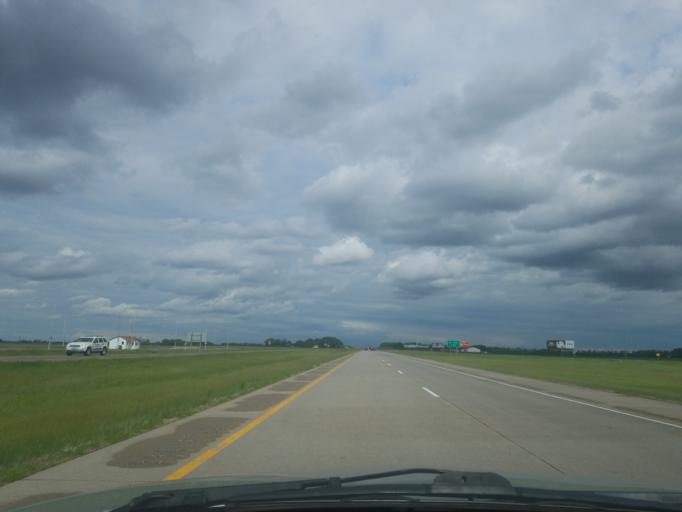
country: US
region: North Dakota
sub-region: Cass County
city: West Fargo
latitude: 46.8774
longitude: -96.9918
